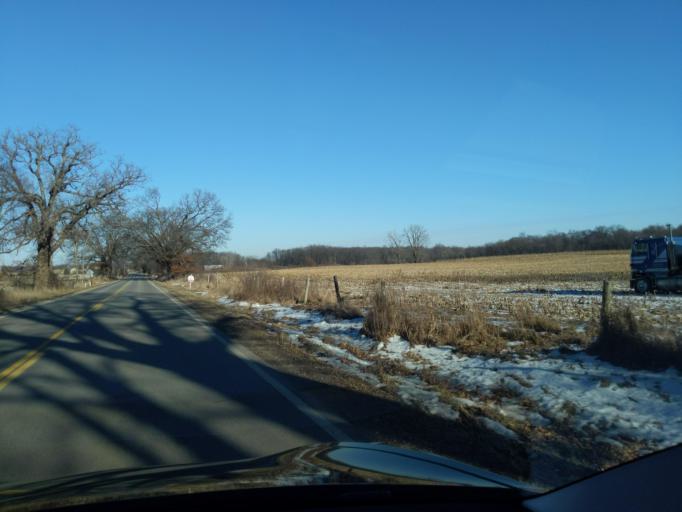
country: US
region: Michigan
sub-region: Ingham County
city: Stockbridge
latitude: 42.4122
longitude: -84.1892
